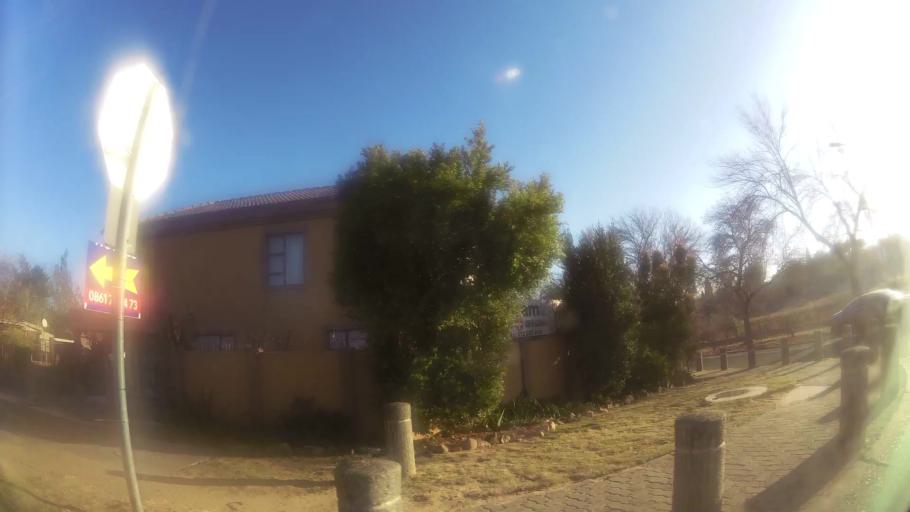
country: ZA
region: Gauteng
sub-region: City of Tshwane Metropolitan Municipality
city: Centurion
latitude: -25.8937
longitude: 28.1360
